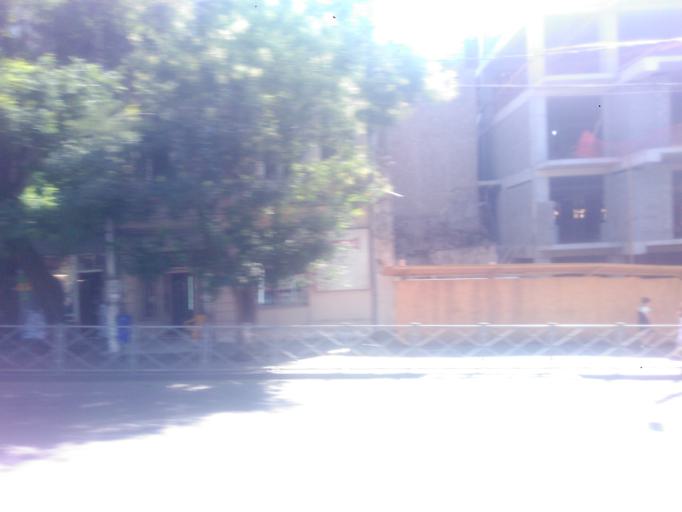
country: GE
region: T'bilisi
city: Tbilisi
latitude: 41.6923
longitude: 44.8136
